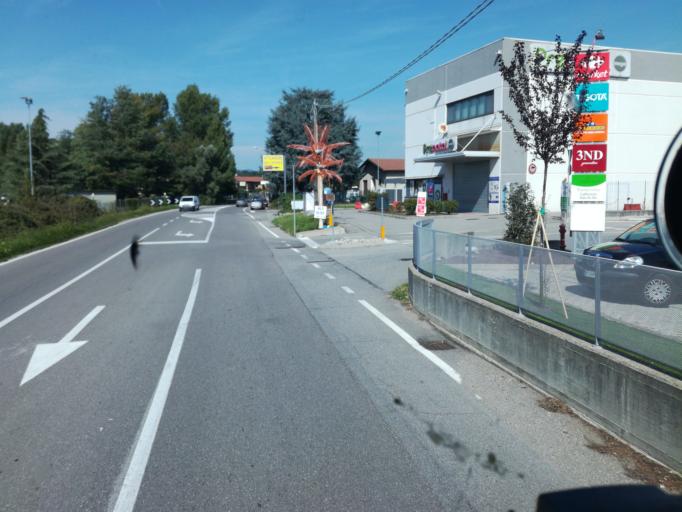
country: IT
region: Lombardy
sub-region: Provincia di Varese
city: Castronno
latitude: 45.7622
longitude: 8.8123
